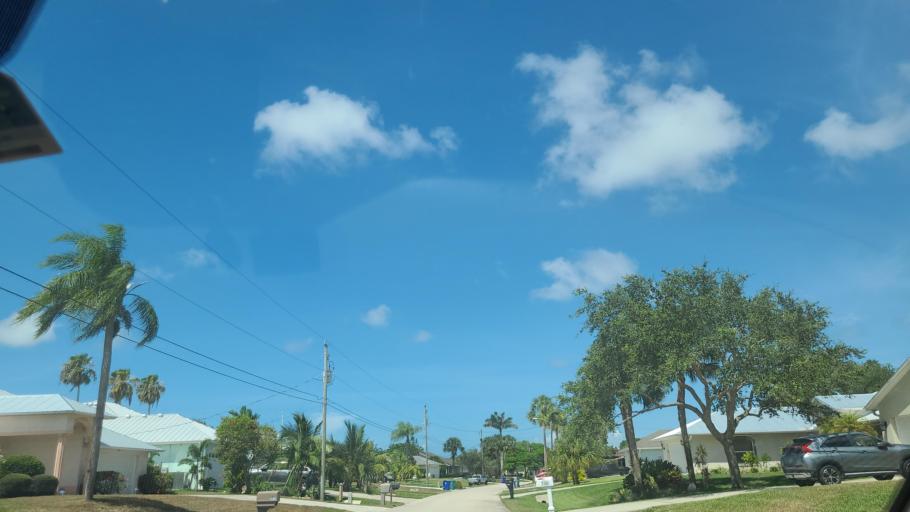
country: US
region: Florida
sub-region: Indian River County
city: Sebastian
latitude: 27.7651
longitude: -80.4749
